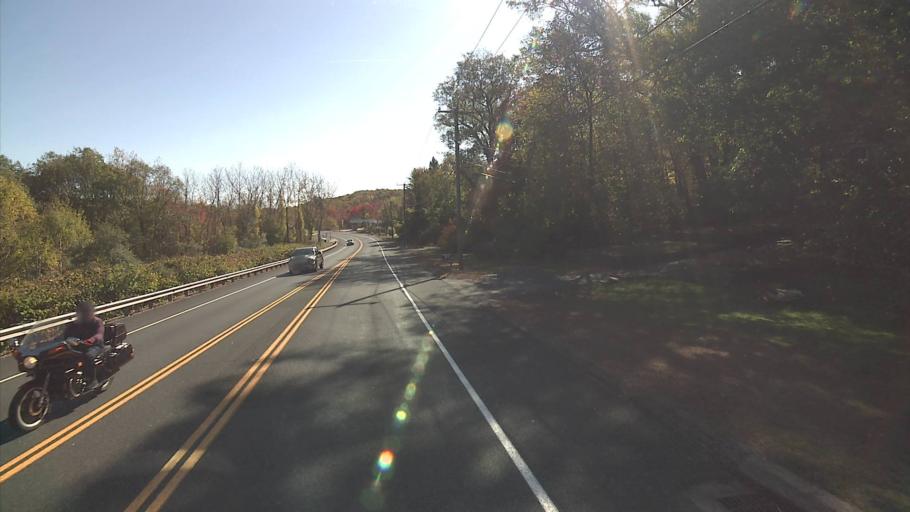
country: US
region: Connecticut
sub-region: Tolland County
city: Rockville
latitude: 41.7852
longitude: -72.4372
